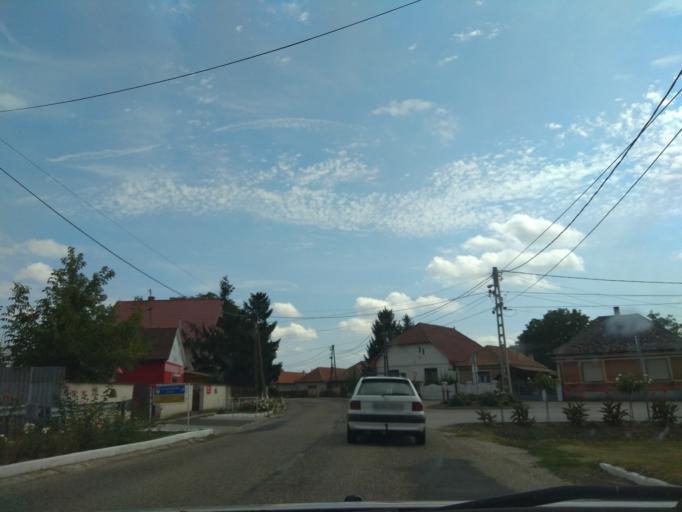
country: HU
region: Borsod-Abauj-Zemplen
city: Sajolad
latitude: 48.0333
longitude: 20.8919
